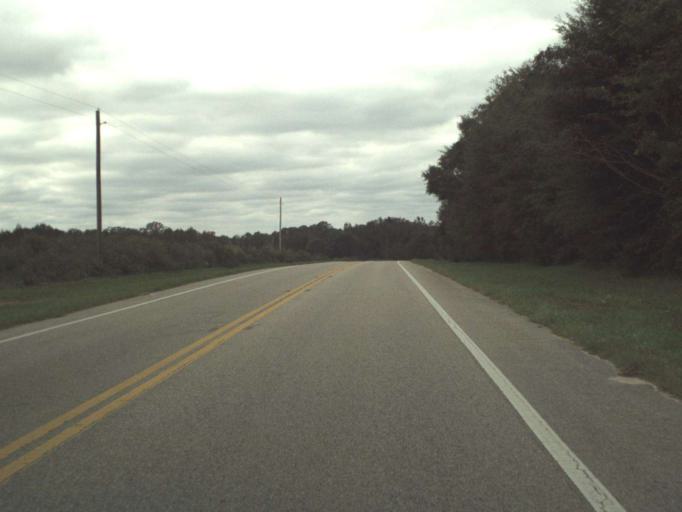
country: US
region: Florida
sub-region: Jackson County
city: Marianna
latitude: 30.6539
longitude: -85.2140
